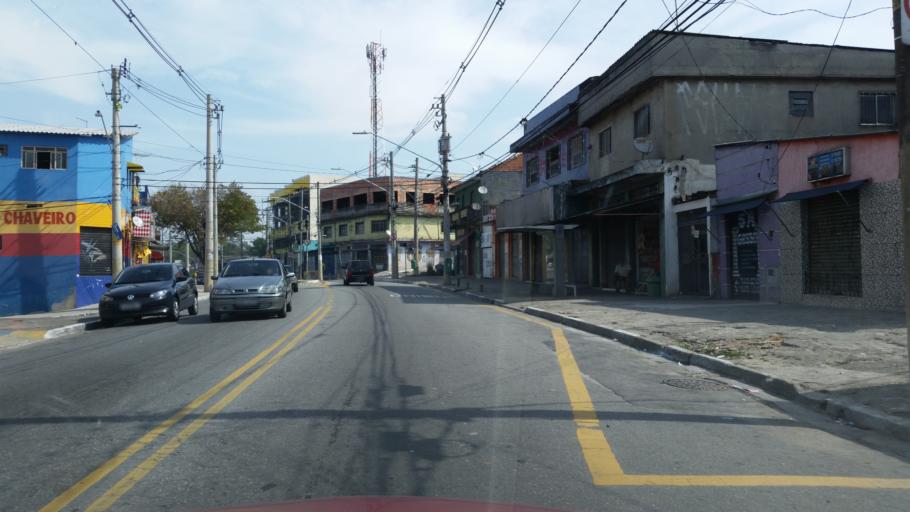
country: BR
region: Sao Paulo
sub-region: Ferraz De Vasconcelos
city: Ferraz de Vasconcelos
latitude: -23.5468
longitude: -46.4264
